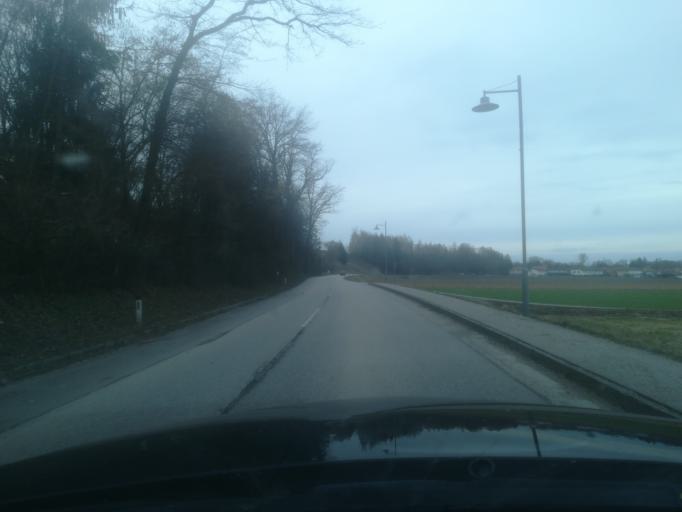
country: AT
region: Upper Austria
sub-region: Wels-Land
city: Gunskirchen
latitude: 48.0811
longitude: 13.9543
